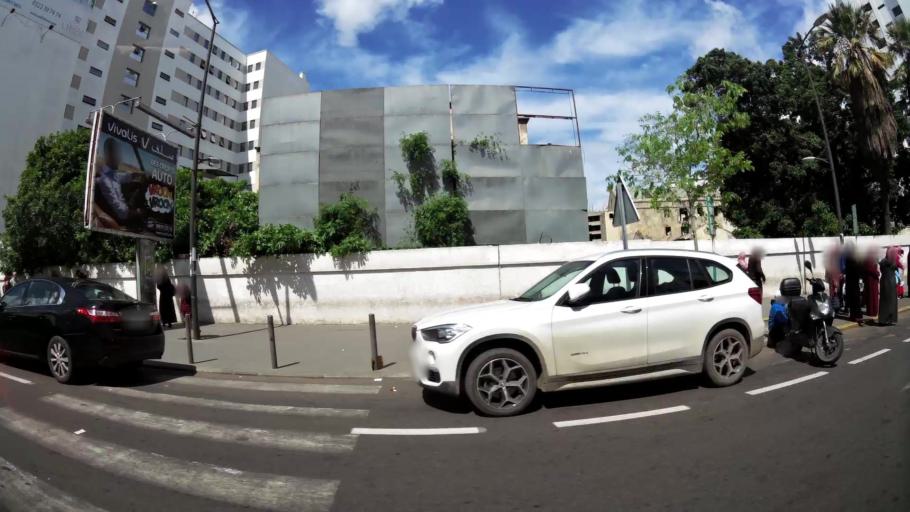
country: MA
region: Grand Casablanca
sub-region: Casablanca
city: Casablanca
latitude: 33.5812
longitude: -7.6246
